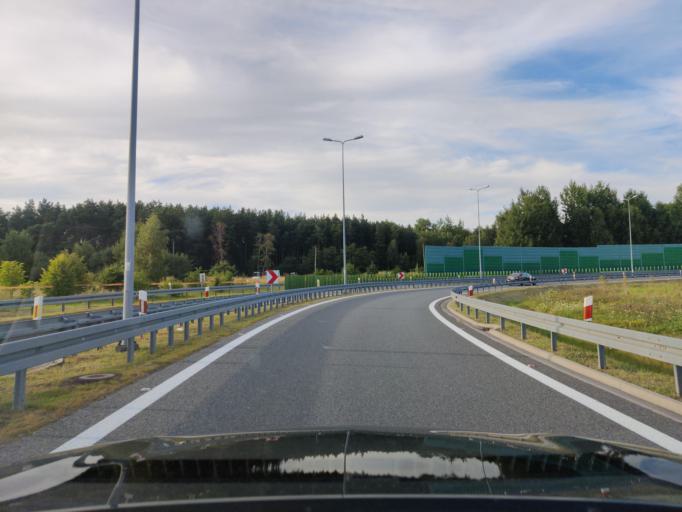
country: PL
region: Masovian Voivodeship
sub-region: Powiat minski
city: Minsk Mazowiecki
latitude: 52.2089
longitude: 21.5289
